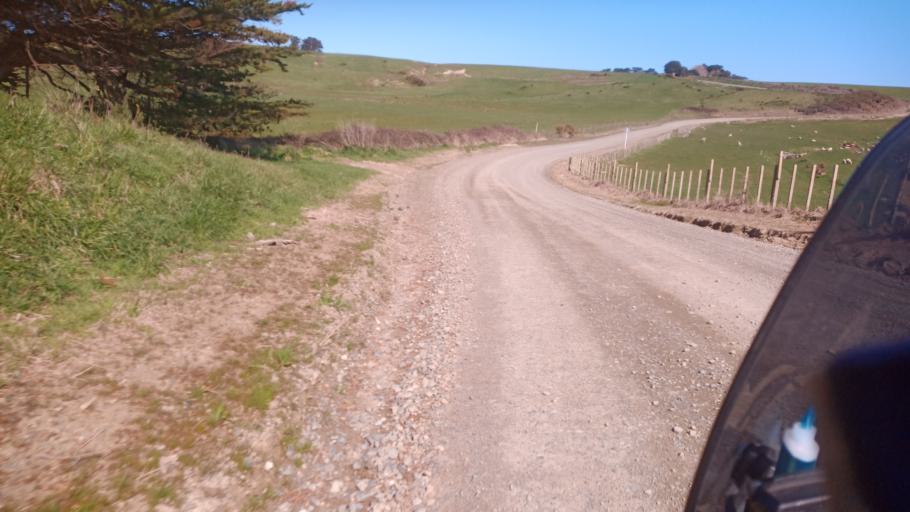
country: NZ
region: Gisborne
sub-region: Gisborne District
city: Gisborne
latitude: -39.1109
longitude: 177.9627
